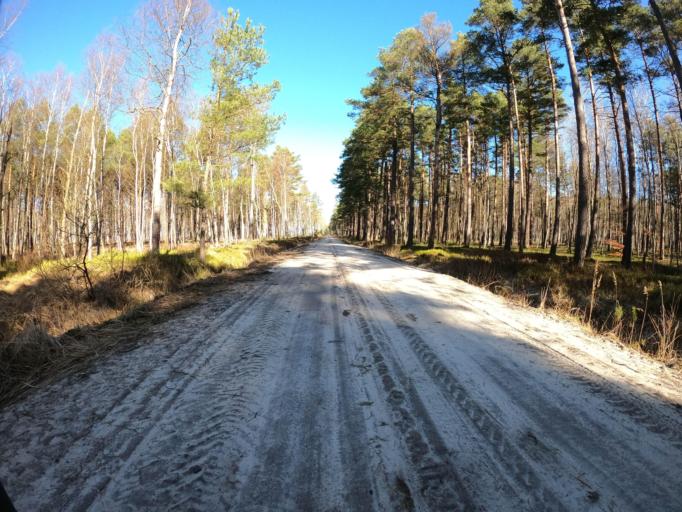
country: PL
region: Greater Poland Voivodeship
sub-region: Powiat zlotowski
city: Sypniewo
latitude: 53.4992
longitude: 16.6409
